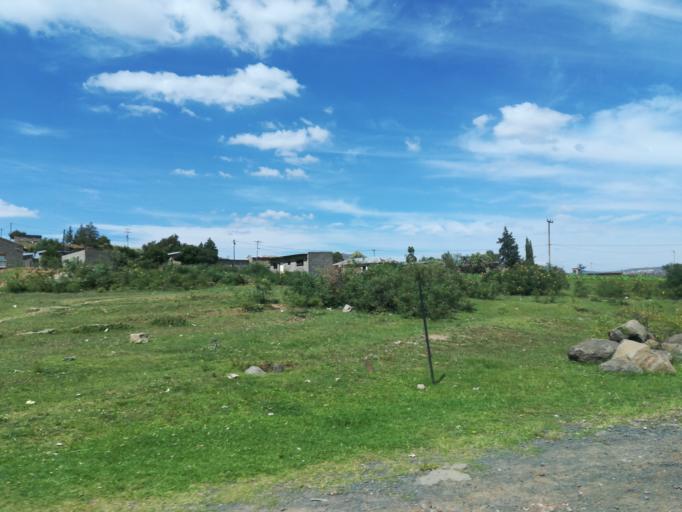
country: LS
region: Mohale's Hoek District
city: Mohale's Hoek
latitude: -30.1068
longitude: 27.4751
